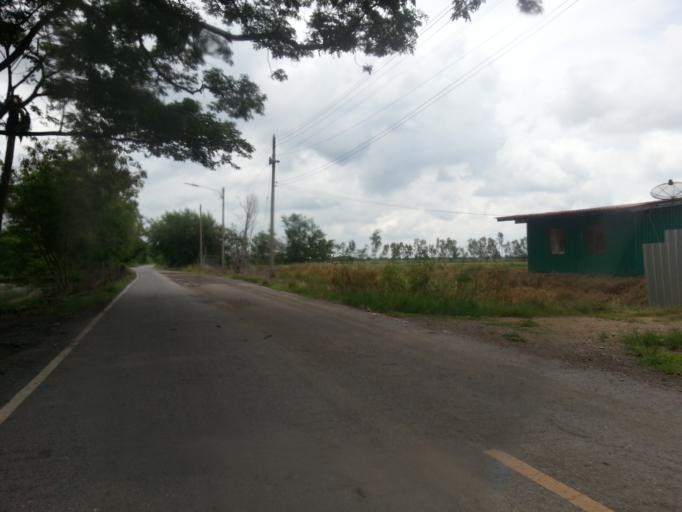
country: TH
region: Pathum Thani
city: Ban Lam Luk Ka
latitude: 14.0100
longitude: 100.8458
